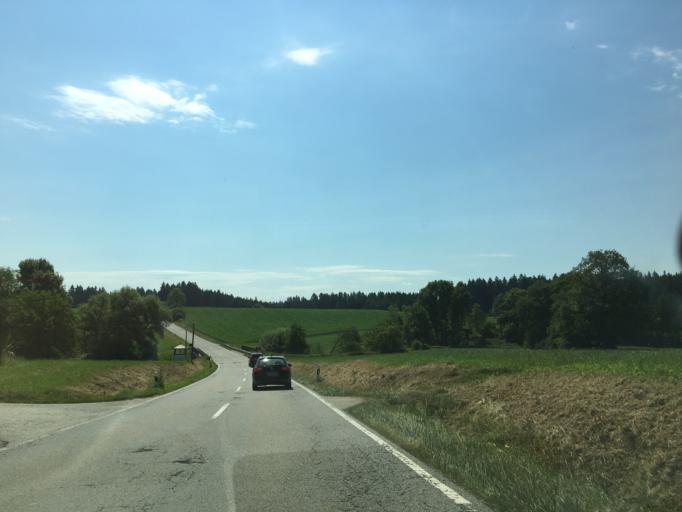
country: DE
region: Bavaria
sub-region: Upper Bavaria
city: Griesstatt
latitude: 47.9810
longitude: 12.2108
